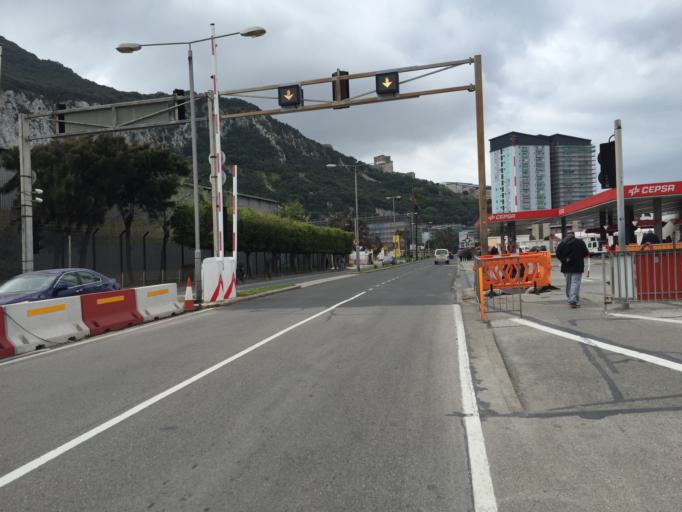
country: GI
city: Gibraltar
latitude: 36.1502
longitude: -5.3489
